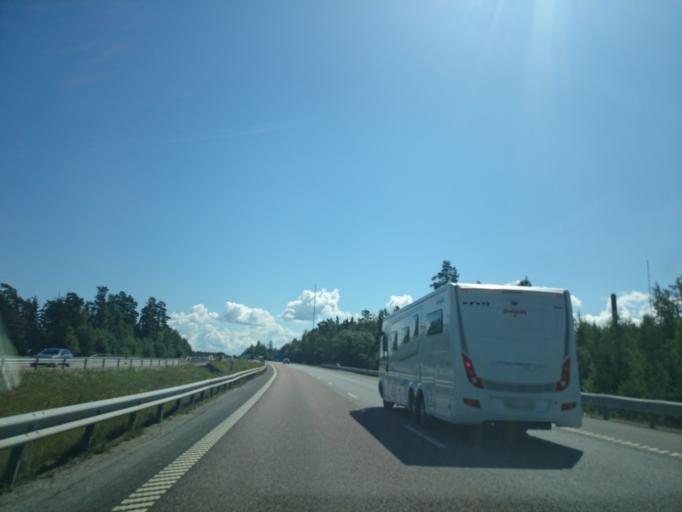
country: SE
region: Gaevleborg
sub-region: Gavle Kommun
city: Gavle
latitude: 60.6450
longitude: 17.1243
